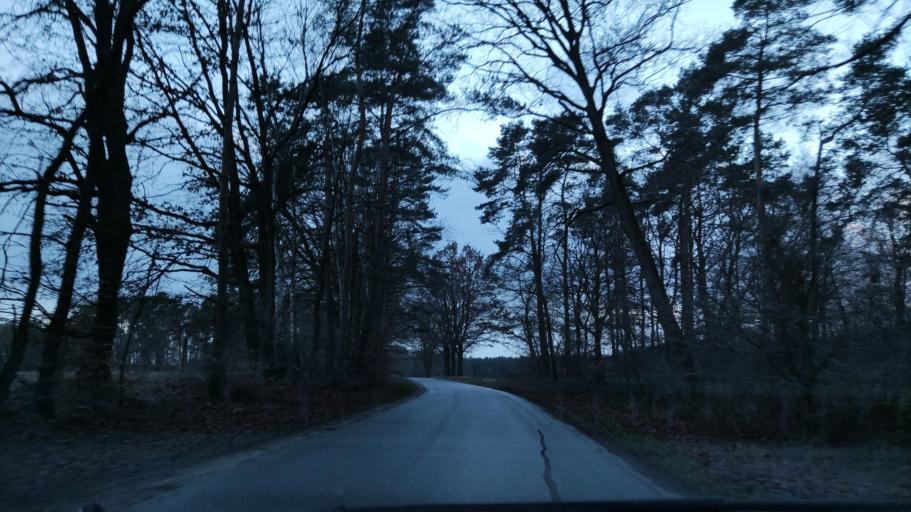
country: DE
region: Lower Saxony
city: Sudergellersen
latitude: 53.2165
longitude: 10.3314
